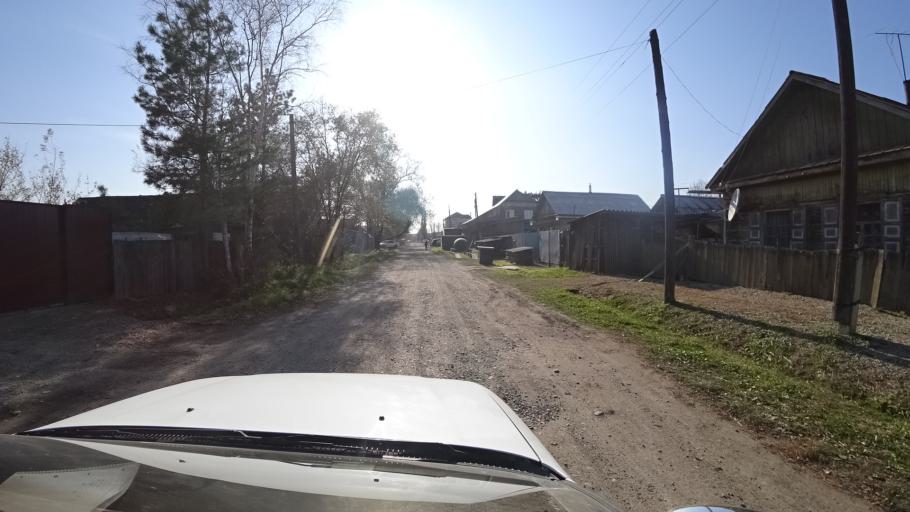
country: RU
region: Primorskiy
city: Dal'nerechensk
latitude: 45.9269
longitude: 133.7253
